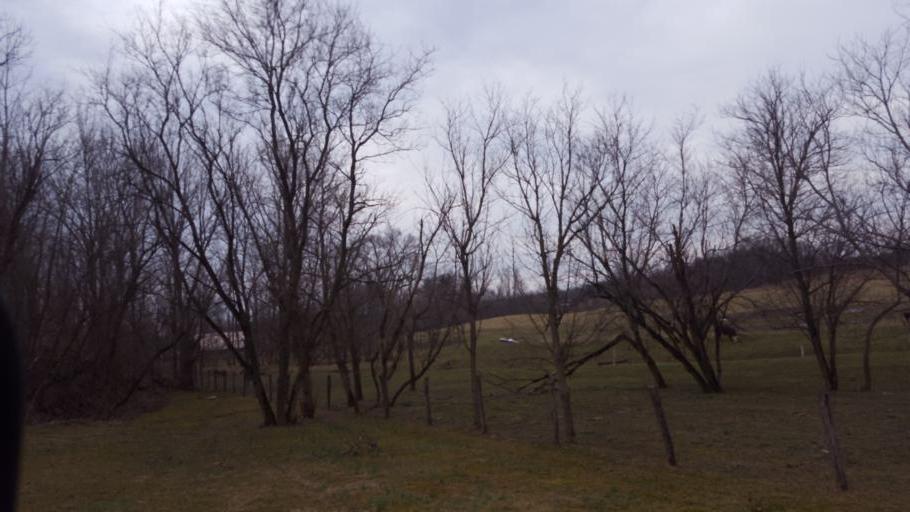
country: US
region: Ohio
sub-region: Ashland County
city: Loudonville
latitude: 40.7011
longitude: -82.2839
